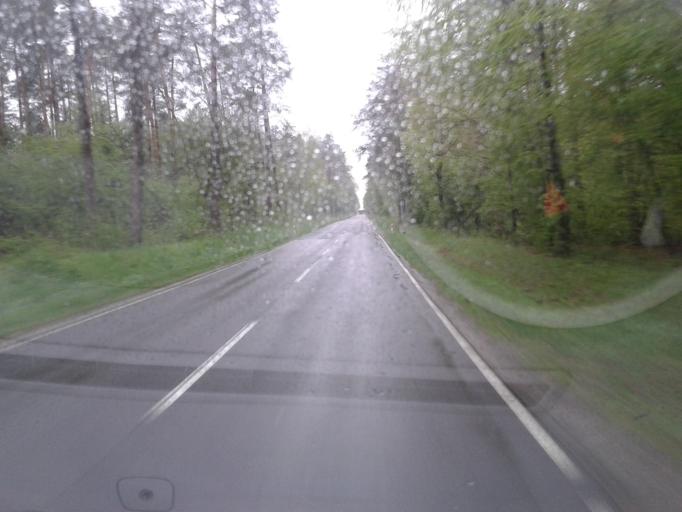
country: PL
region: Subcarpathian Voivodeship
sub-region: Powiat lubaczowski
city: Nowe Siolo
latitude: 50.2965
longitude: 23.2075
